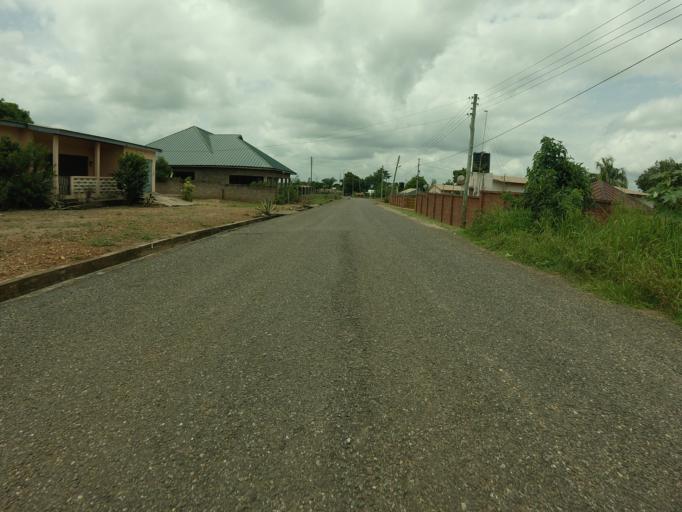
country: GH
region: Volta
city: Ho
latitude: 6.5898
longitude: 0.4782
